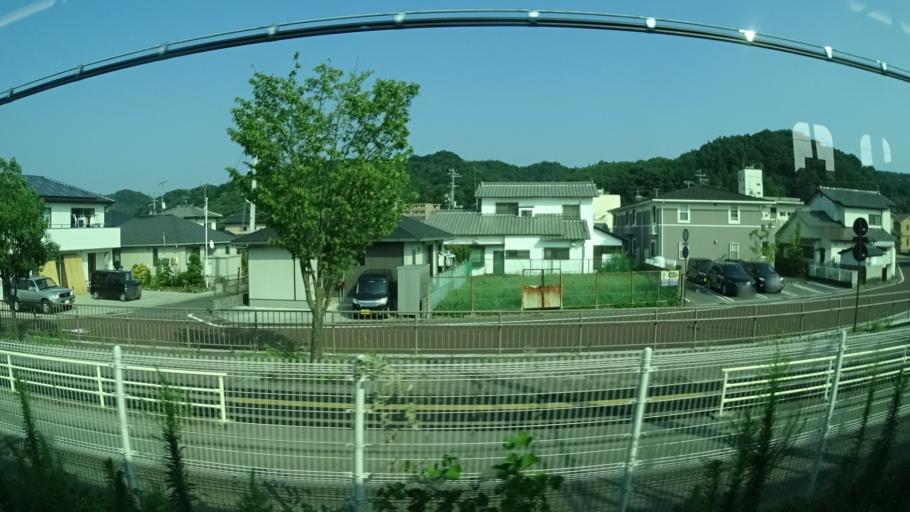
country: JP
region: Fukushima
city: Iwaki
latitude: 37.0377
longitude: 140.8567
